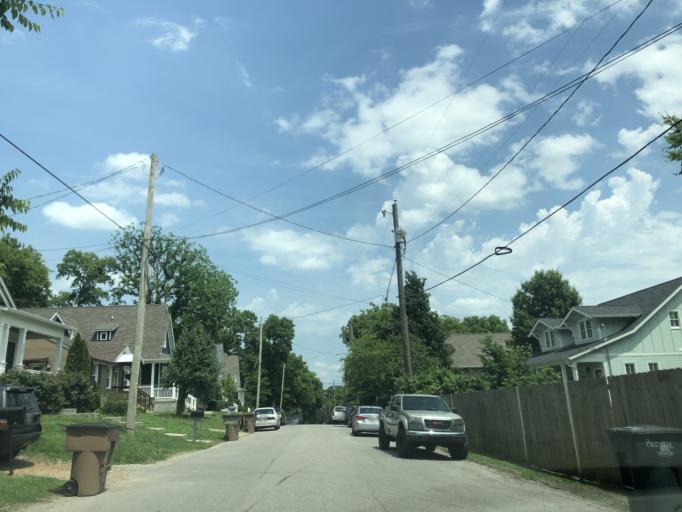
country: US
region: Tennessee
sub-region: Davidson County
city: Nashville
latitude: 36.1734
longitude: -86.7500
